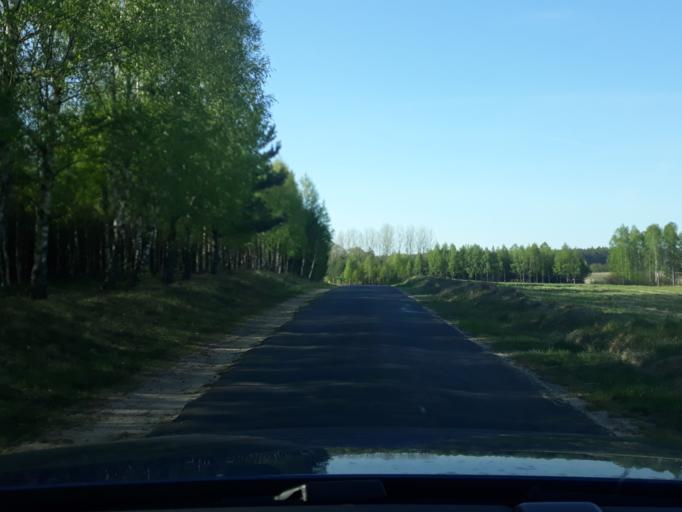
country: PL
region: Pomeranian Voivodeship
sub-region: Powiat czluchowski
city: Przechlewo
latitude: 53.8677
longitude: 17.3340
